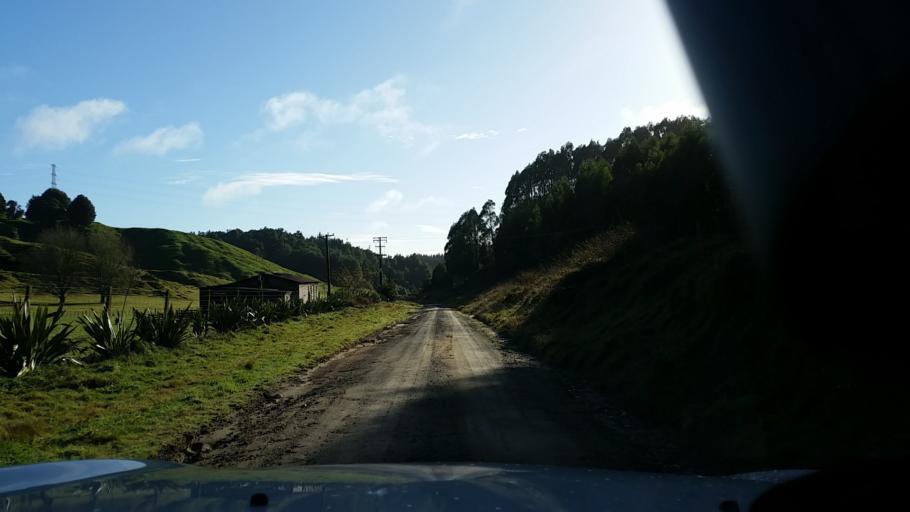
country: NZ
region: Bay of Plenty
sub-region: Kawerau District
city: Kawerau
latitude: -38.0149
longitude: 176.5971
